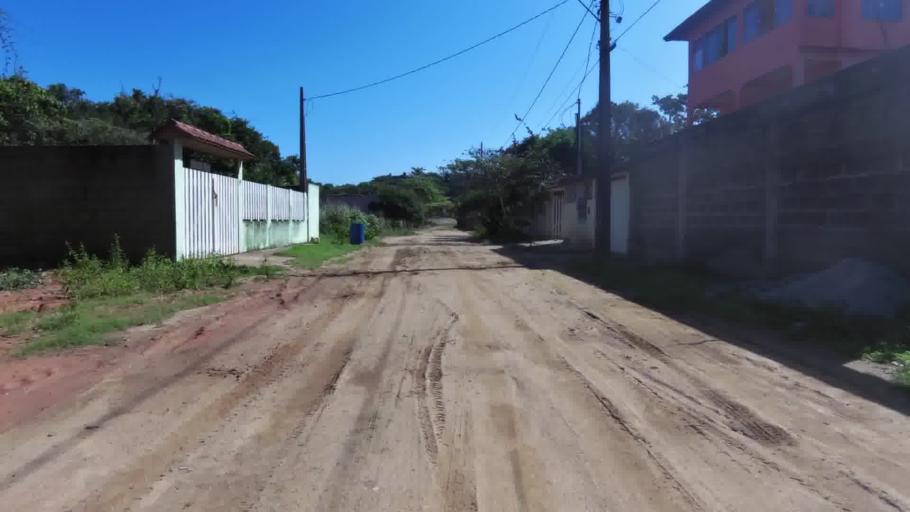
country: BR
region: Espirito Santo
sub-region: Piuma
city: Piuma
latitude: -20.8265
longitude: -40.6185
